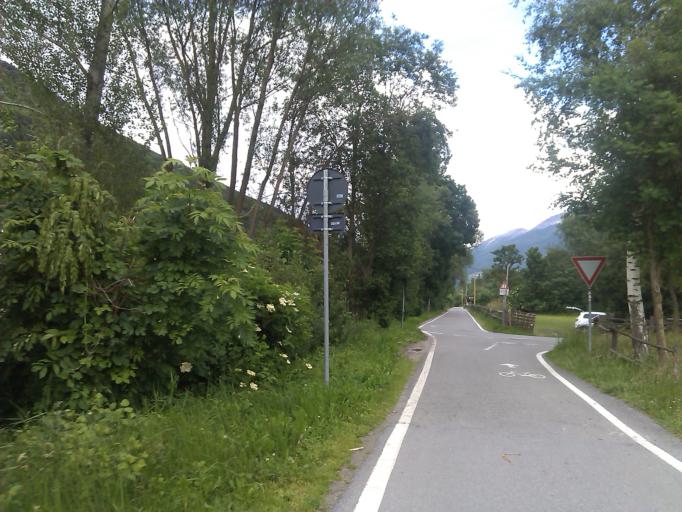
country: IT
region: Trentino-Alto Adige
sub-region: Bolzano
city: Prato Allo Stelvio
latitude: 46.6368
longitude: 10.6009
